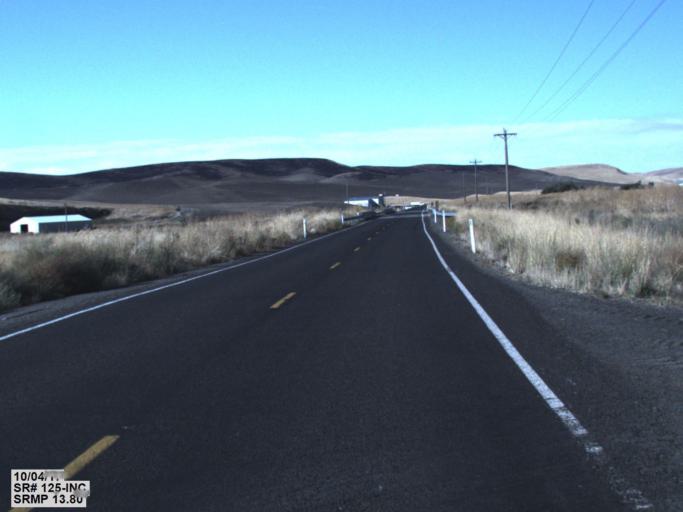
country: US
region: Washington
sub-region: Walla Walla County
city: Walla Walla
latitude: 46.1687
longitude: -118.3827
